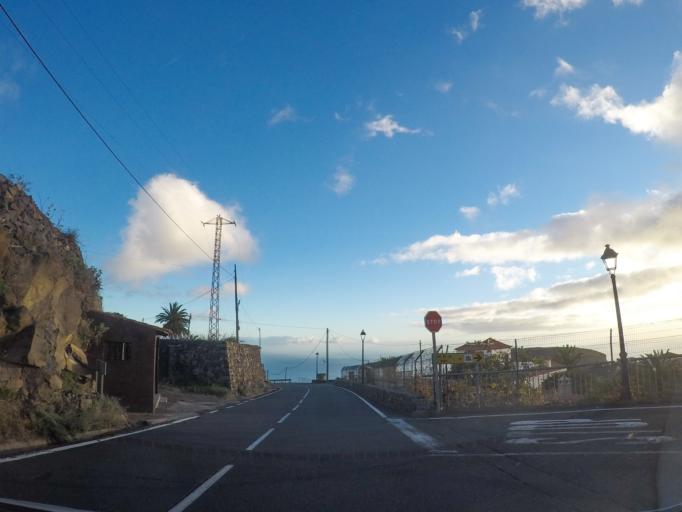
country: ES
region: Canary Islands
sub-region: Provincia de Santa Cruz de Tenerife
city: Alajero
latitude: 28.0623
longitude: -17.2371
